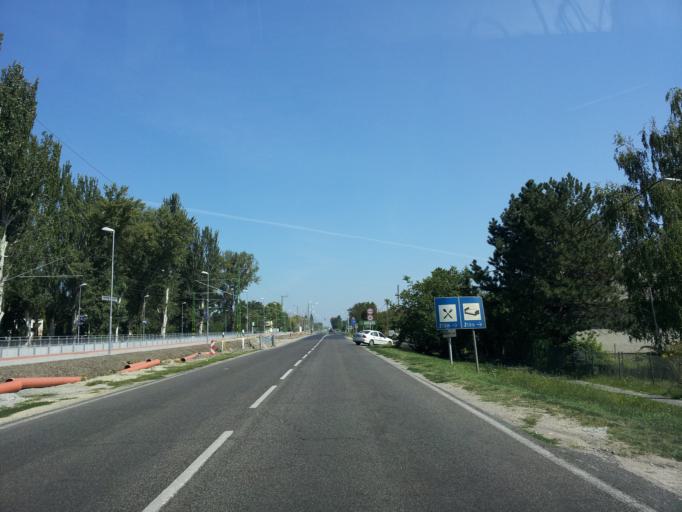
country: HU
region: Somogy
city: Zamardi
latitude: 46.8907
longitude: 17.9898
